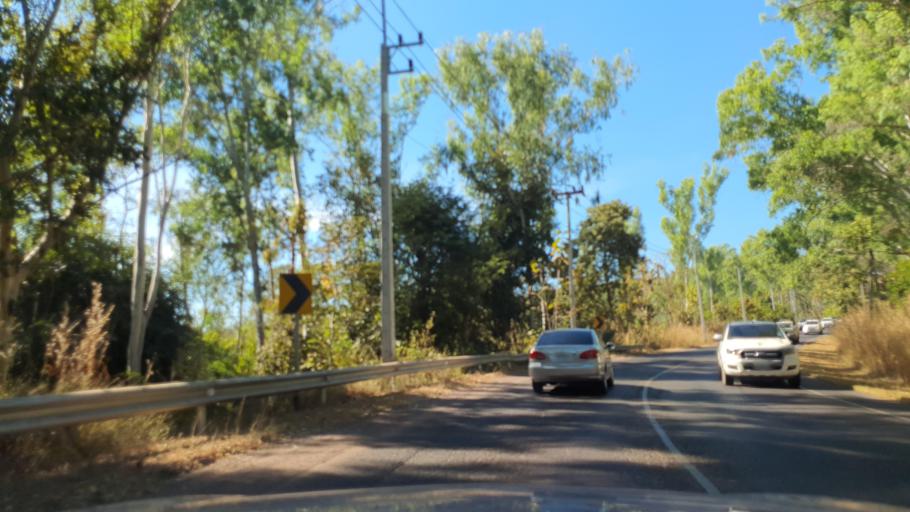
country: TH
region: Kalasin
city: Khao Wong
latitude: 16.7640
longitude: 104.1410
